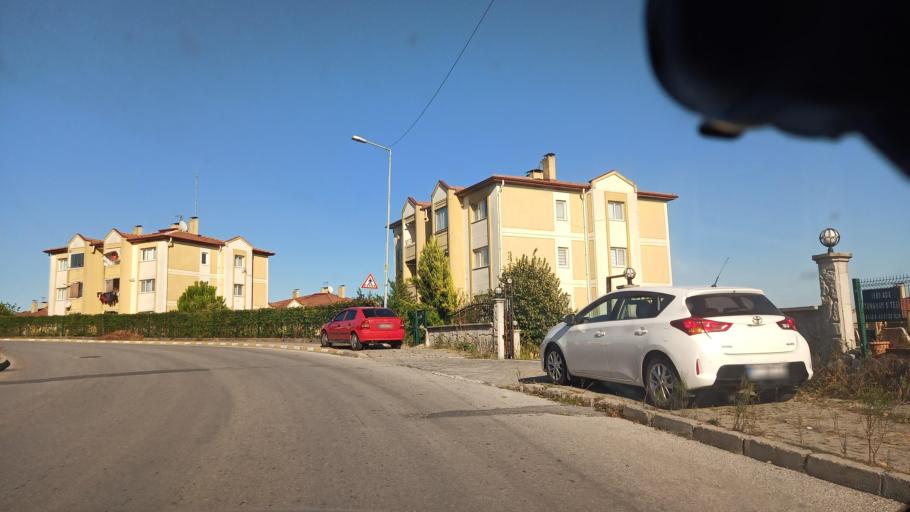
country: TR
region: Sakarya
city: Kazimpasa
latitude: 40.8554
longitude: 30.2939
